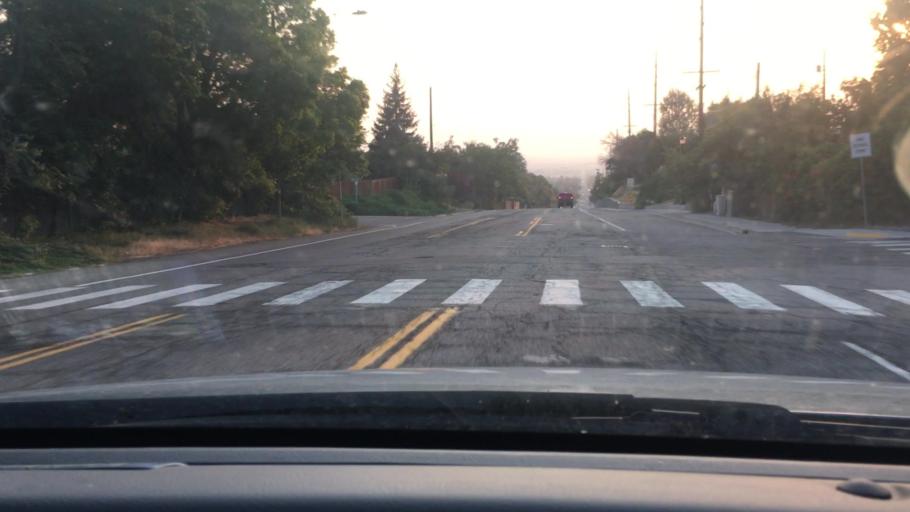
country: US
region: Utah
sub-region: Salt Lake County
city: East Millcreek
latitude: 40.6871
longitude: -111.8054
